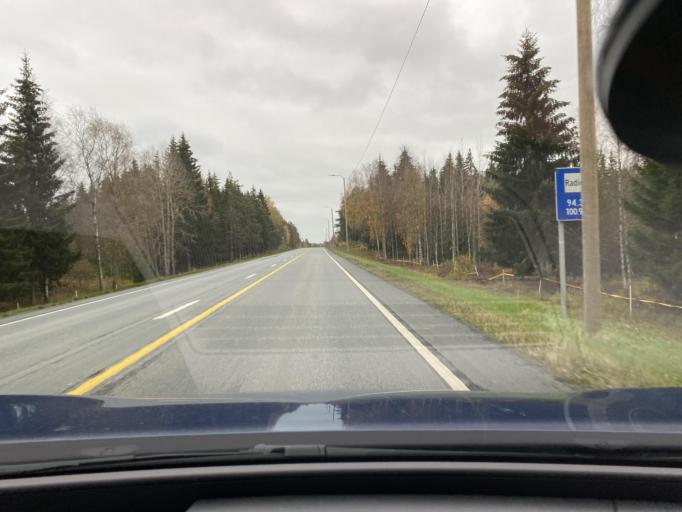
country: FI
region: Varsinais-Suomi
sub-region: Vakka-Suomi
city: Laitila
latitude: 60.9459
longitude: 21.6003
